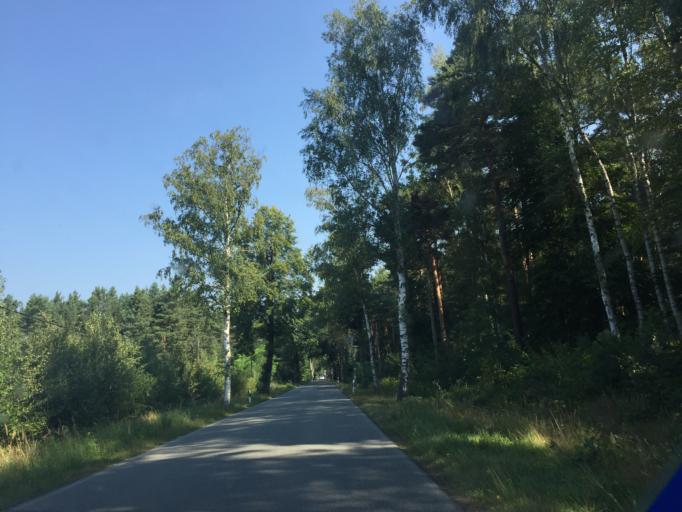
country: DE
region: Saxony
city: Uhyst
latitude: 51.3529
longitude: 14.5064
